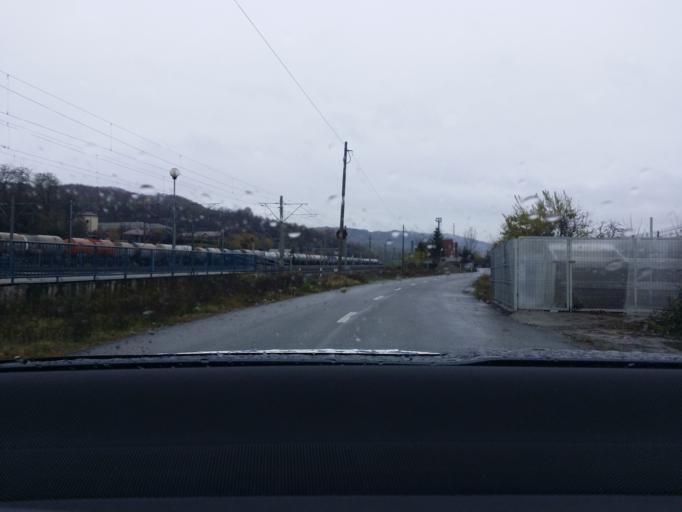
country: RO
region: Prahova
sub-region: Comuna Cornu
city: Cornu de Jos
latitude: 45.1338
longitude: 25.7092
